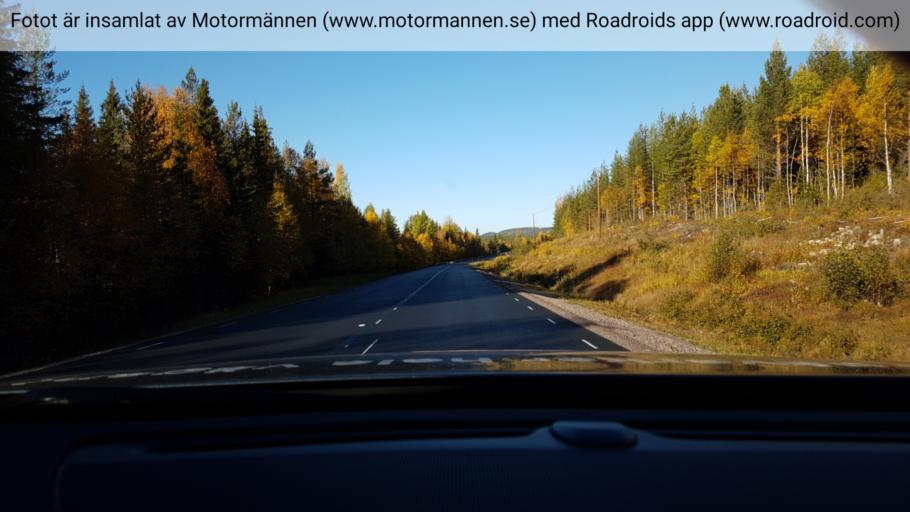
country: SE
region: Vaesterbotten
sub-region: Norsjo Kommun
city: Norsjoe
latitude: 65.4037
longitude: 19.9291
